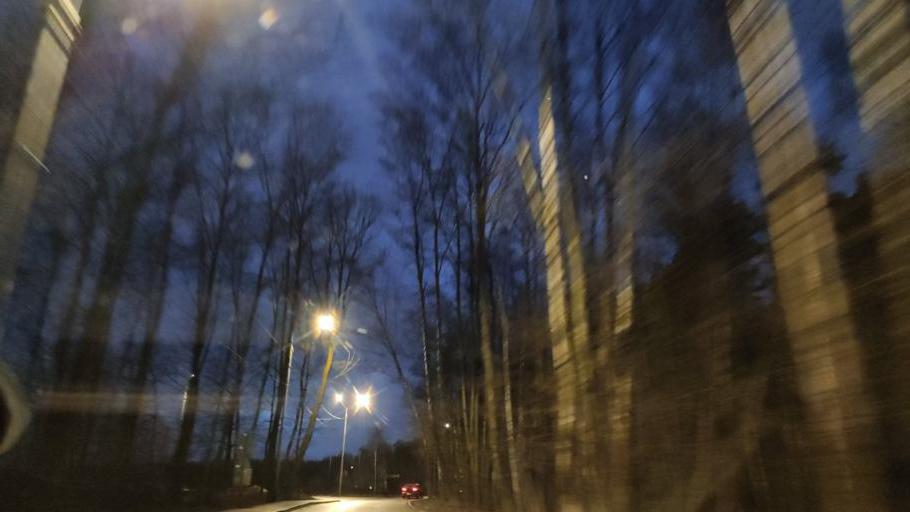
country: RU
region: Moskovskaya
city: Biryulevo Zapadnoye
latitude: 55.5582
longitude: 37.6369
